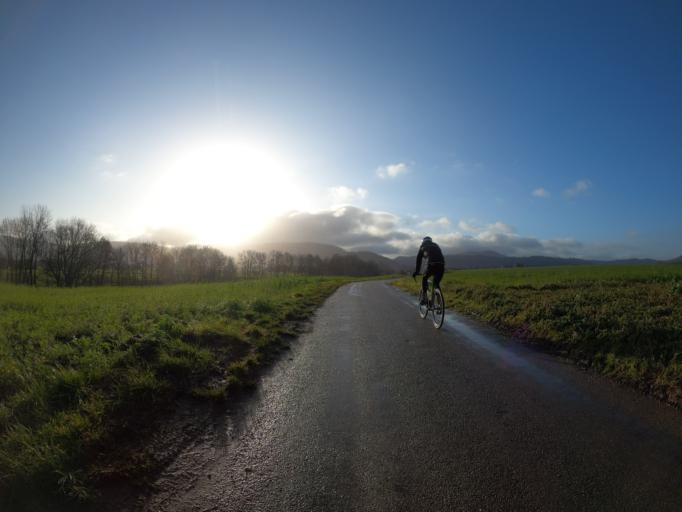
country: DE
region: Baden-Wuerttemberg
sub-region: Regierungsbezirk Stuttgart
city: Boll
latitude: 48.6505
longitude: 9.6214
